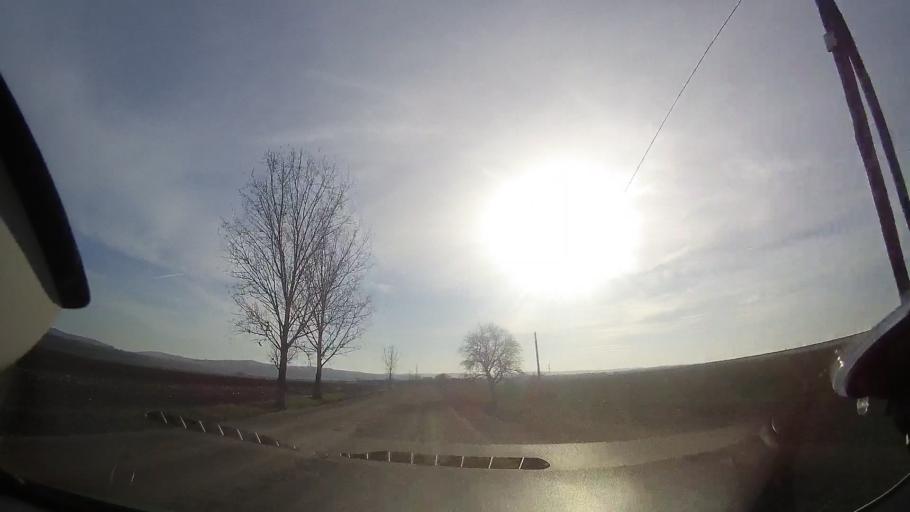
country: RO
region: Bihor
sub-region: Comuna Ciuhoiu
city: Ciuhoiu
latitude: 47.2215
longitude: 22.1345
